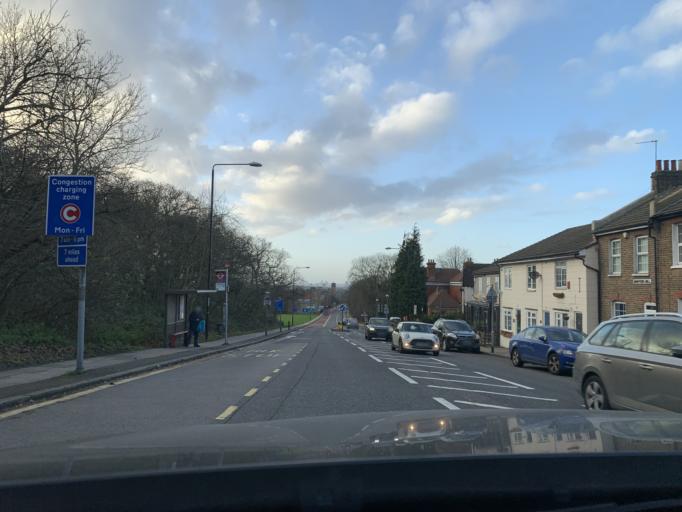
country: GB
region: England
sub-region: Greater London
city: Woolwich
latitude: 51.4704
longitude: 0.0597
